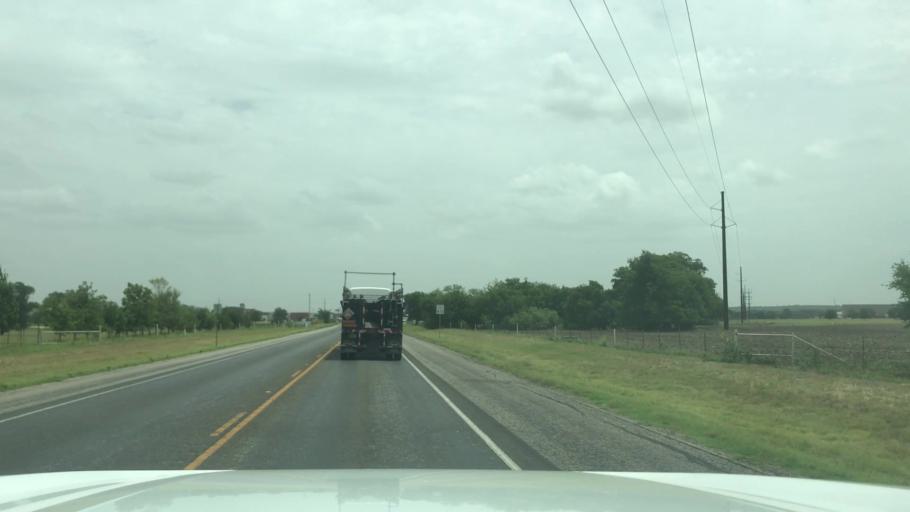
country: US
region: Texas
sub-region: Bosque County
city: Clifton
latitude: 31.7981
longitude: -97.5941
